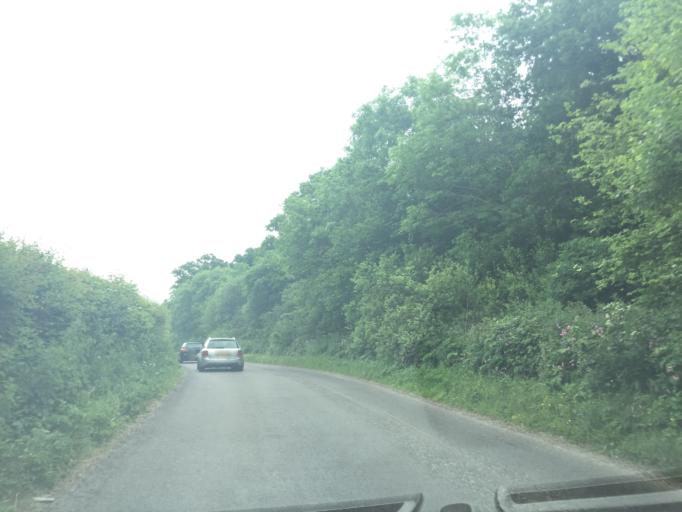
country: GB
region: England
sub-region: Dorset
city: Wool
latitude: 50.6486
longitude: -2.2702
